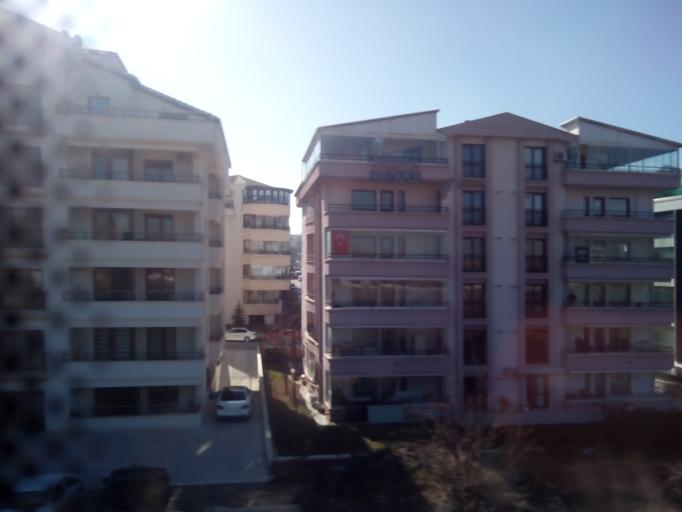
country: TR
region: Ankara
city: Batikent
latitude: 39.9167
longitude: 32.7705
